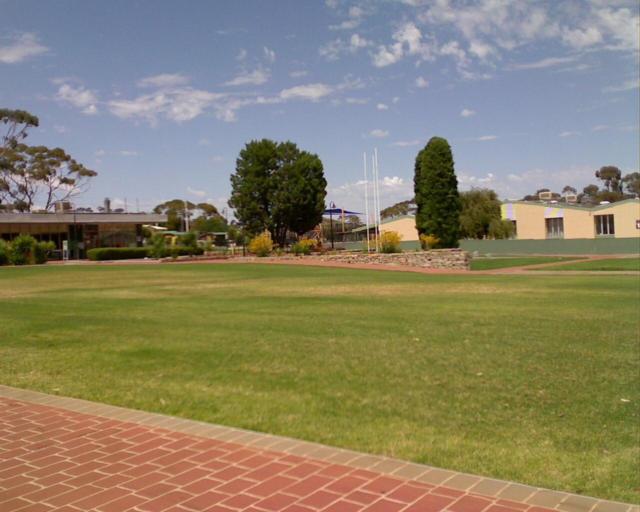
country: AU
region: Western Australia
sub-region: Kalgoorlie/Boulder
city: Stoneville
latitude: -31.2039
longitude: 121.6676
